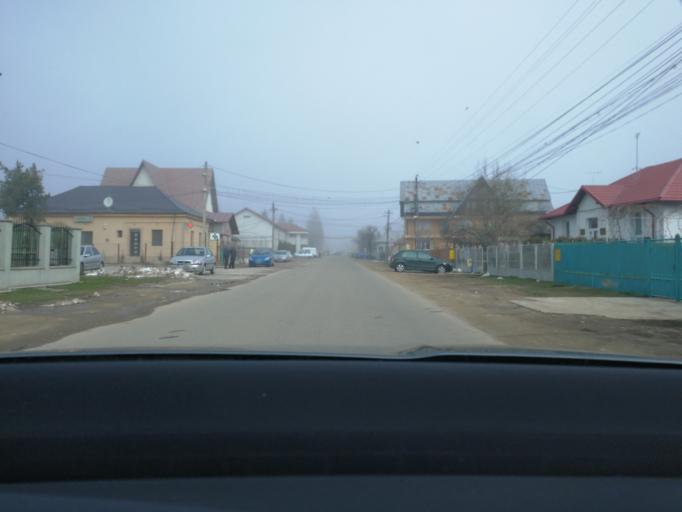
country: RO
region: Prahova
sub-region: Comuna Magureni
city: Lunca Prahovei
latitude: 45.0422
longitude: 25.7525
